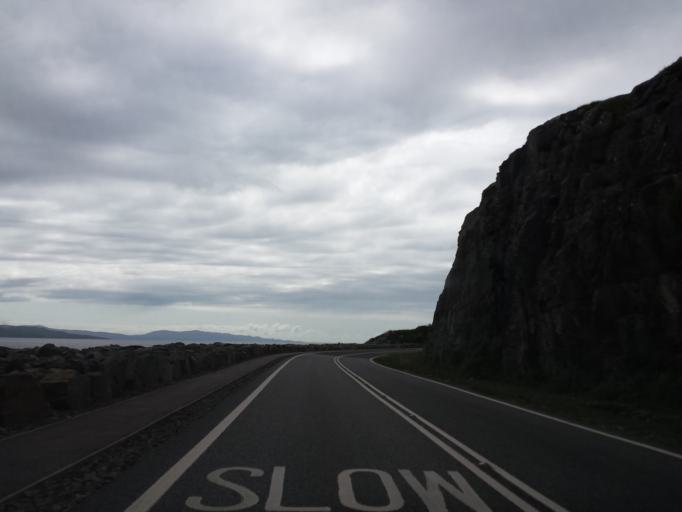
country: GB
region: Scotland
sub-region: Argyll and Bute
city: Isle Of Mull
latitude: 56.8940
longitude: -5.7534
